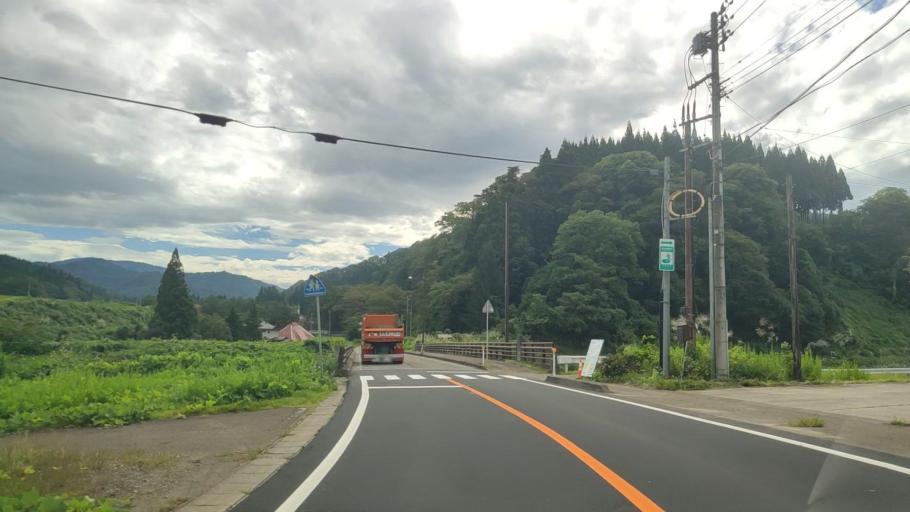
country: JP
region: Niigata
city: Arai
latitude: 36.9573
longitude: 138.2705
